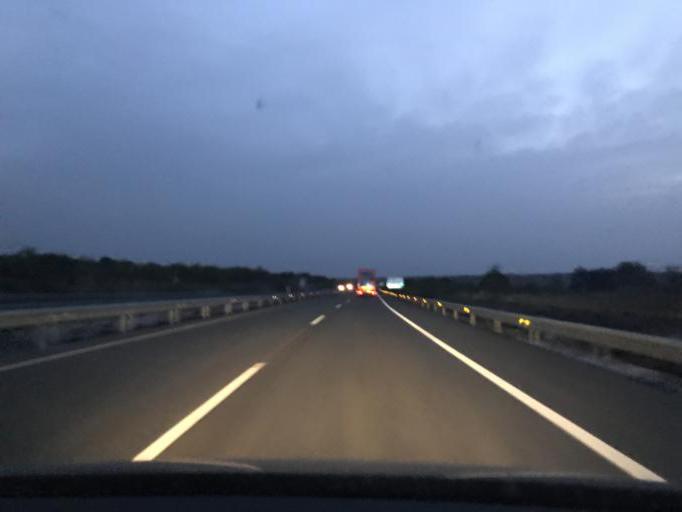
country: ES
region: Andalusia
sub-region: Provincia de Granada
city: Gor
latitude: 37.4014
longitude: -2.9308
